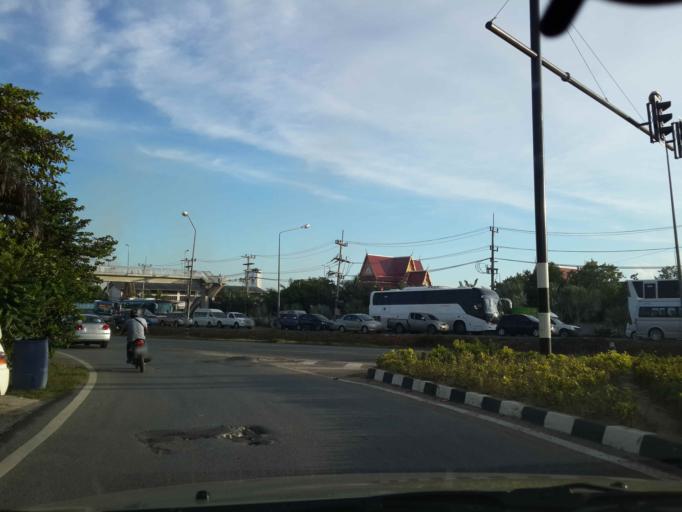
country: TH
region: Chon Buri
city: Phatthaya
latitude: 12.8575
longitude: 100.9091
